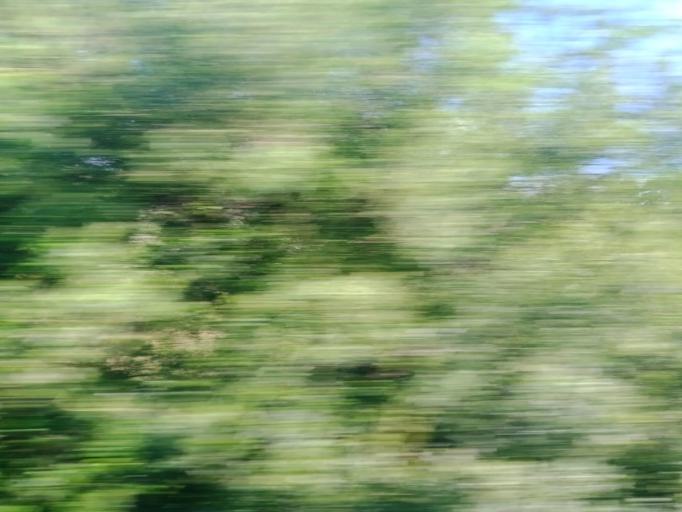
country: GB
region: Wales
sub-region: Gwynedd
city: Aber
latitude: 53.2325
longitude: -4.0400
